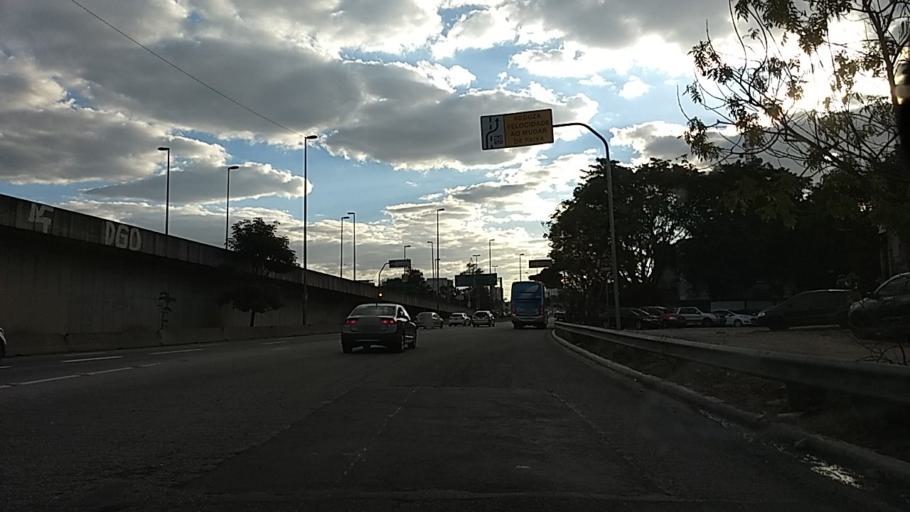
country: BR
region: Sao Paulo
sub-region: Sao Paulo
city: Sao Paulo
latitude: -23.5278
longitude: -46.5913
